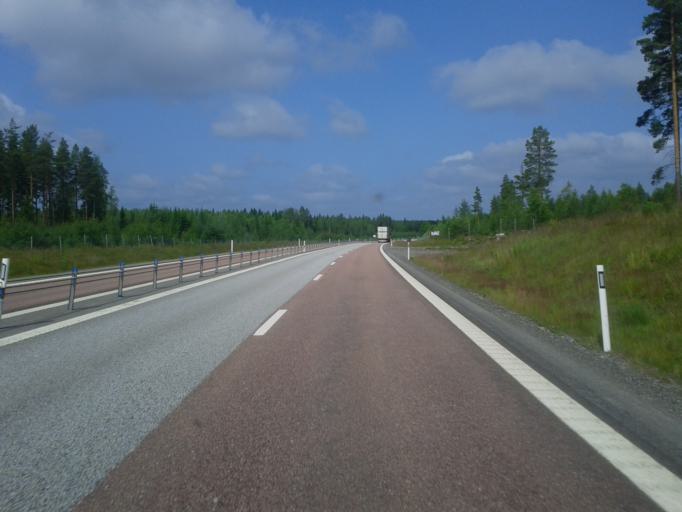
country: SE
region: Vaesterbotten
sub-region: Skelleftea Kommun
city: Skelleftea
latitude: 64.6988
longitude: 21.0085
